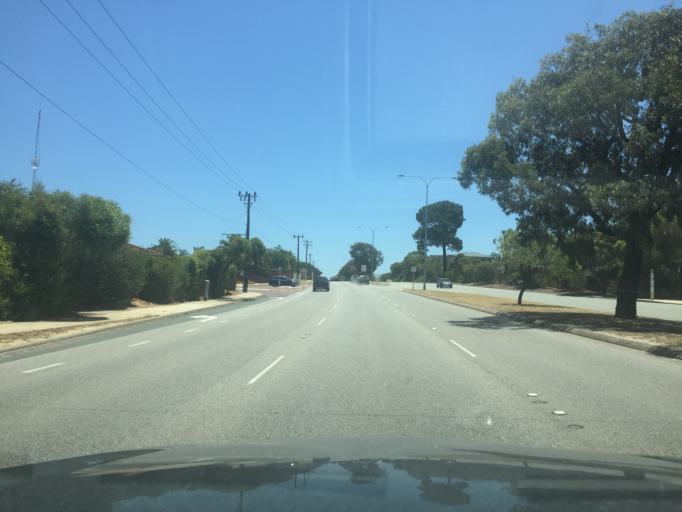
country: AU
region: Western Australia
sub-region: Melville
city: Kardinya
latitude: -32.0673
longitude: 115.8088
